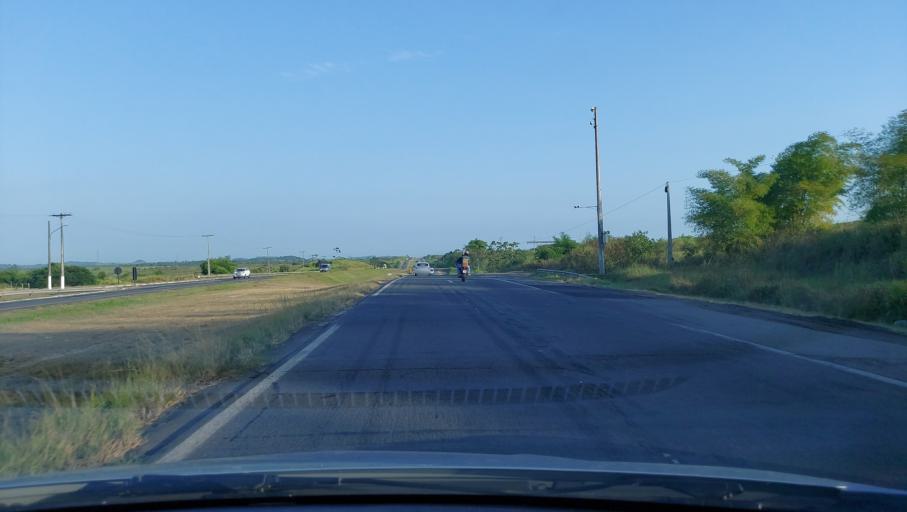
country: BR
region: Bahia
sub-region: Santo Amaro
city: Santo Amaro
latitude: -12.5138
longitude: -38.6249
